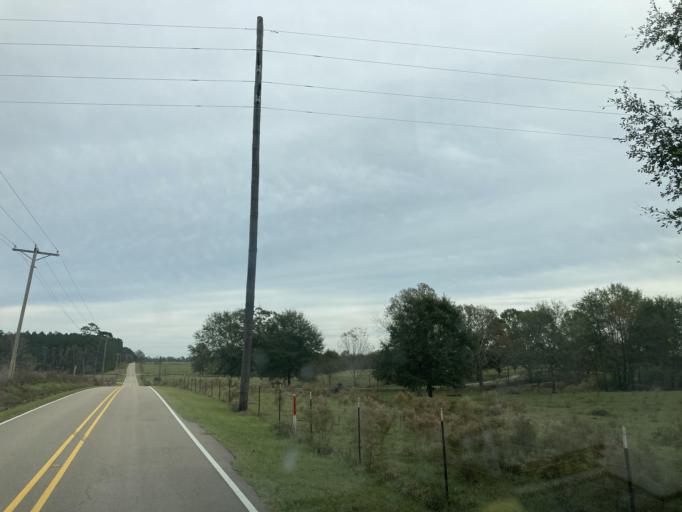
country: US
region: Mississippi
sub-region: Lamar County
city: Lumberton
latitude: 31.0394
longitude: -89.4207
